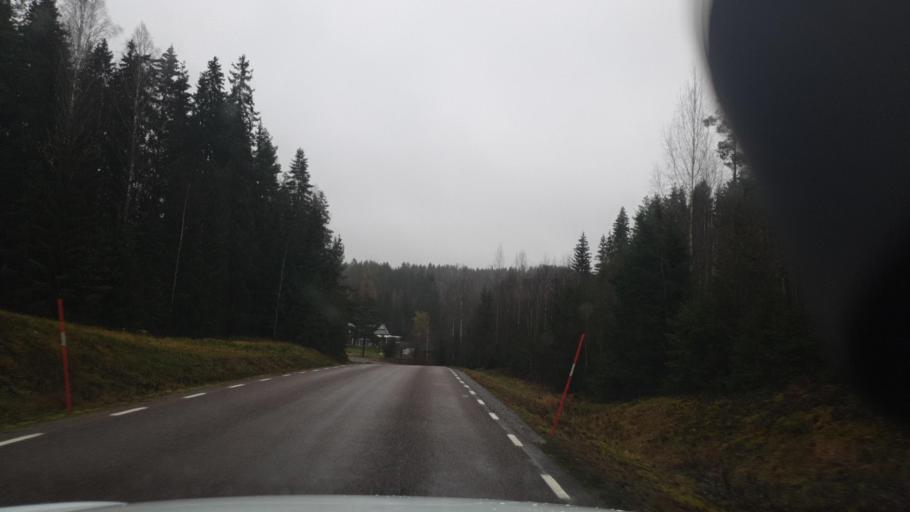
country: SE
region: Vaermland
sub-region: Arvika Kommun
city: Arvika
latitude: 59.6151
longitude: 12.7844
